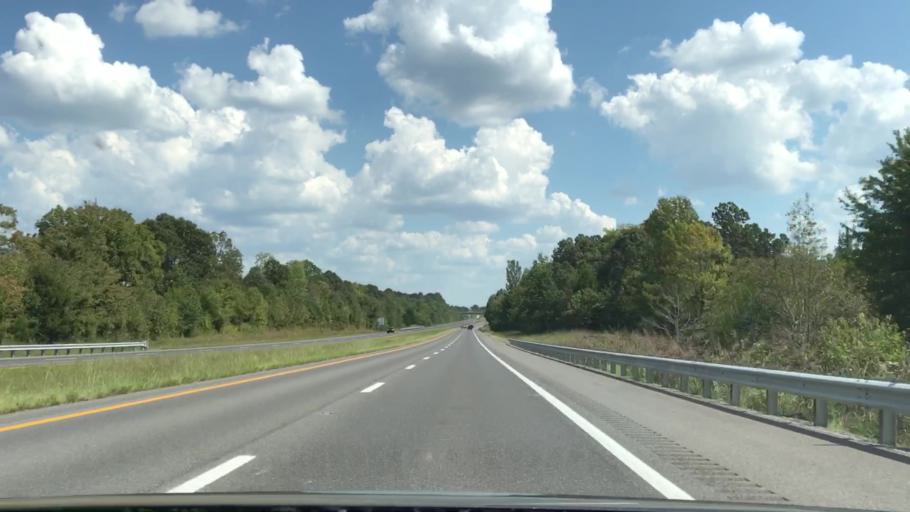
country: US
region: Kentucky
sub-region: Lyon County
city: Eddyville
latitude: 37.1093
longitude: -88.0117
